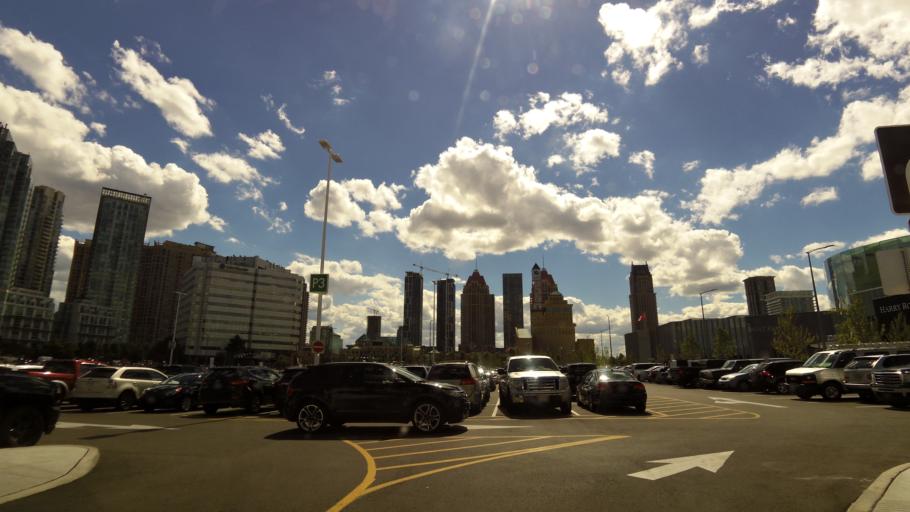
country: CA
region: Ontario
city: Mississauga
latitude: 43.5915
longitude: -79.6412
